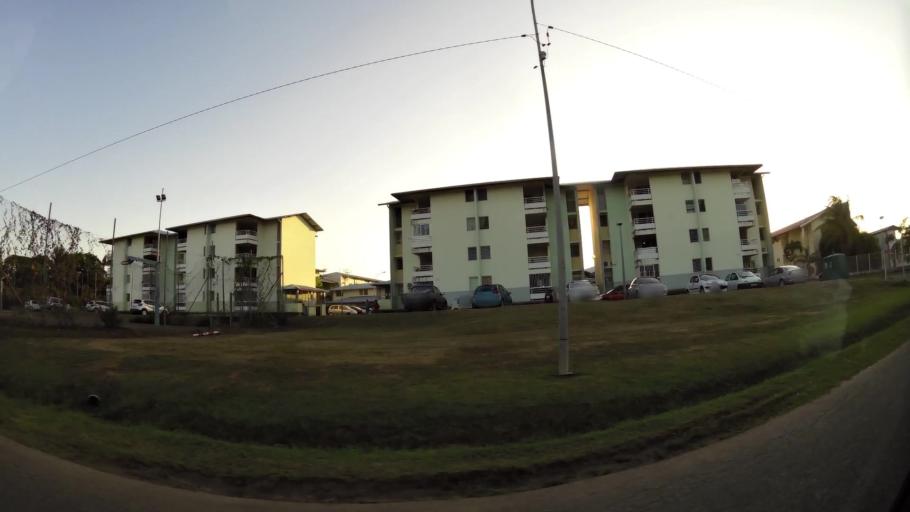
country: GF
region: Guyane
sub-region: Guyane
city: Cayenne
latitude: 4.9276
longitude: -52.3036
